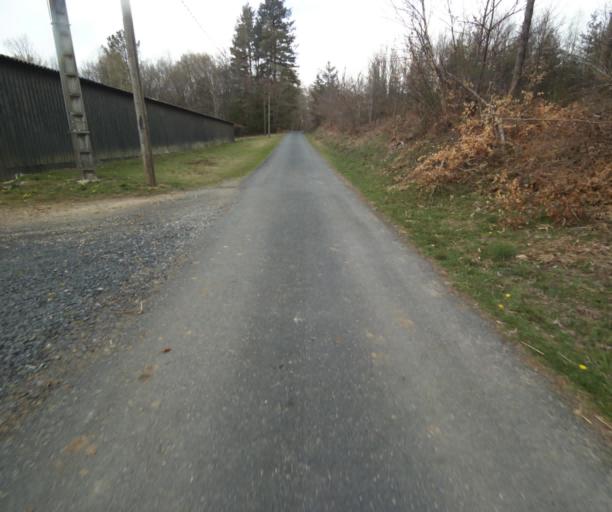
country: FR
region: Limousin
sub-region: Departement de la Correze
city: Correze
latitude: 45.2758
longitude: 1.9510
